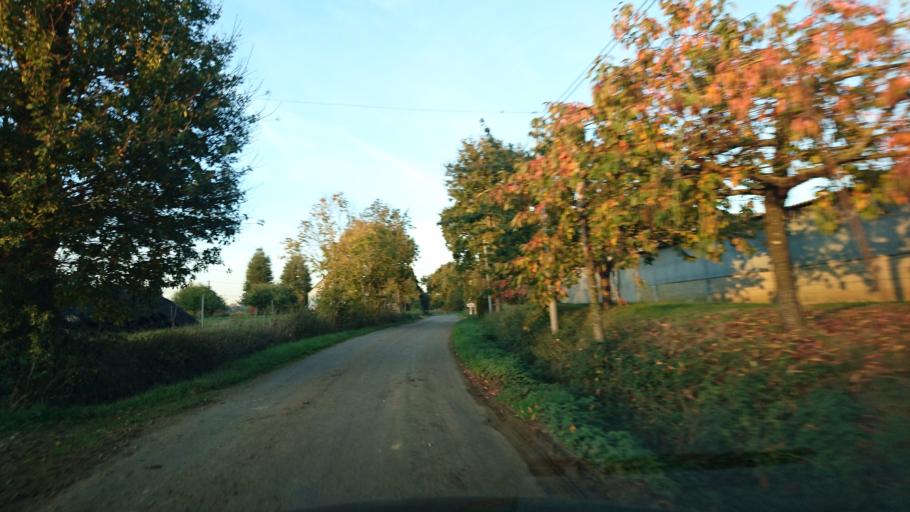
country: FR
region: Brittany
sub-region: Departement d'Ille-et-Vilaine
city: Bruz
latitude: 48.0068
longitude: -1.7552
